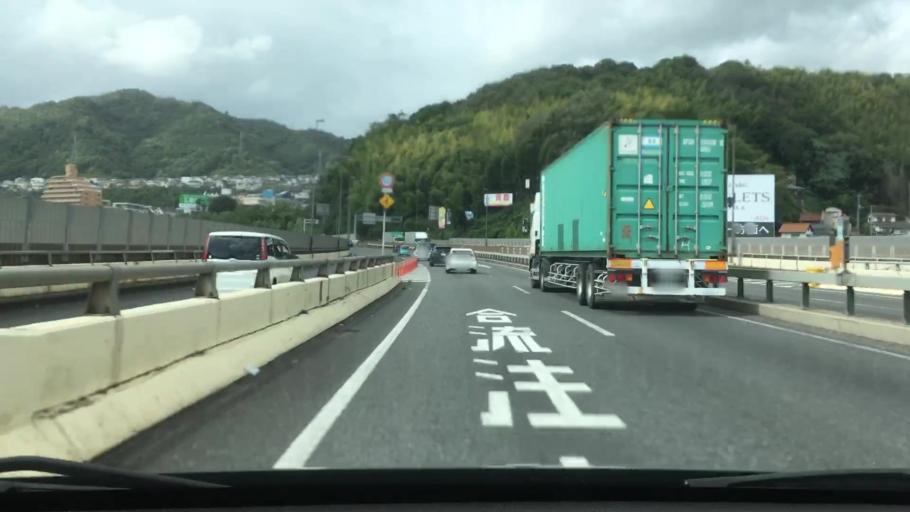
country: JP
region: Hiroshima
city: Hiroshima-shi
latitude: 34.3931
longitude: 132.4215
